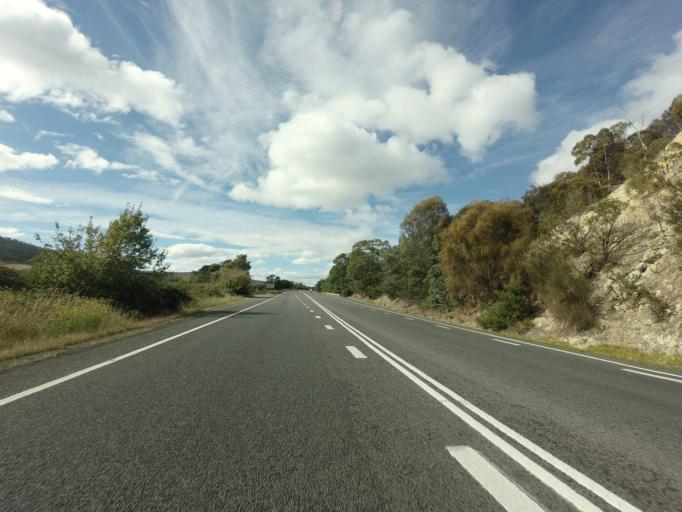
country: AU
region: Tasmania
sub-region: Glenorchy
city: Granton
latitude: -42.7551
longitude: 147.1612
